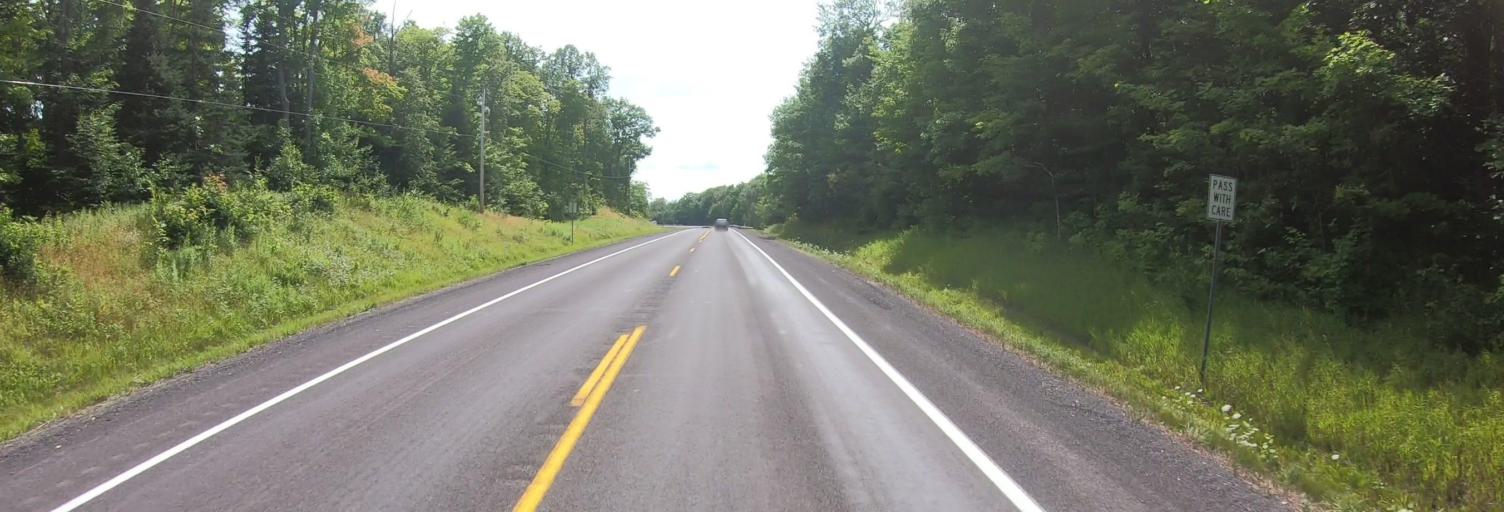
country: US
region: Michigan
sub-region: Houghton County
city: Hancock
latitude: 46.9942
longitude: -88.7763
